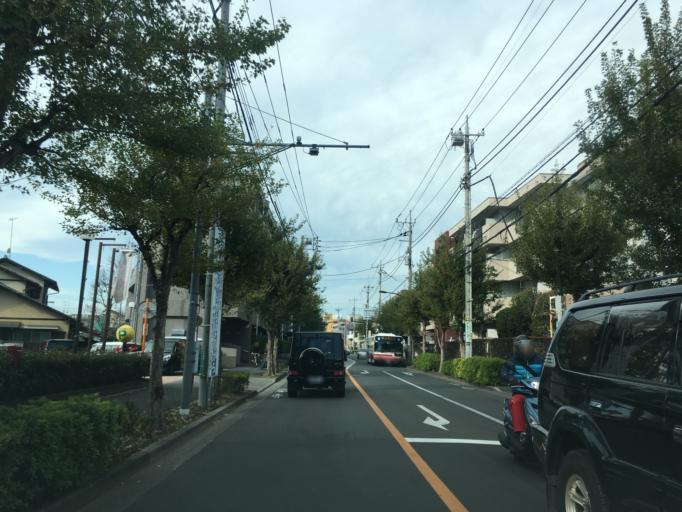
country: JP
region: Tokyo
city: Chofugaoka
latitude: 35.6380
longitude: 139.5743
